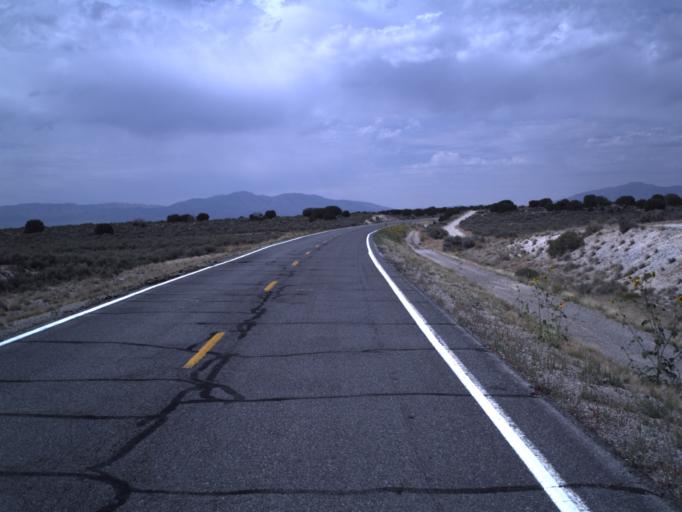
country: US
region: Utah
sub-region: Utah County
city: Eagle Mountain
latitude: 40.2311
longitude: -112.1869
